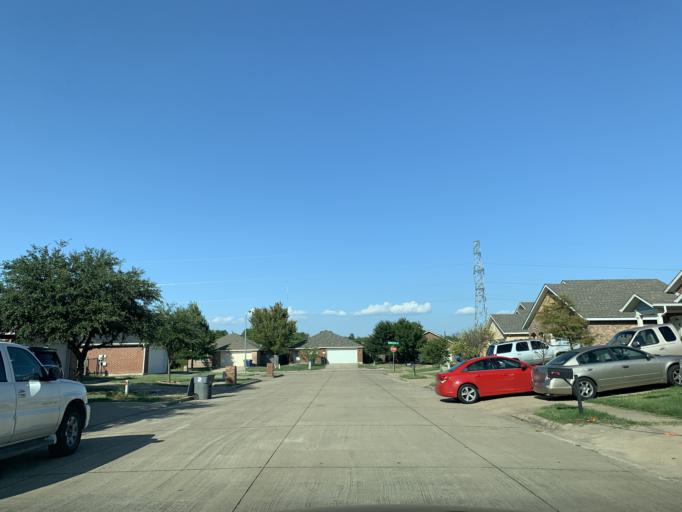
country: US
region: Texas
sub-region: Dallas County
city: Hutchins
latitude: 32.6546
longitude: -96.7657
